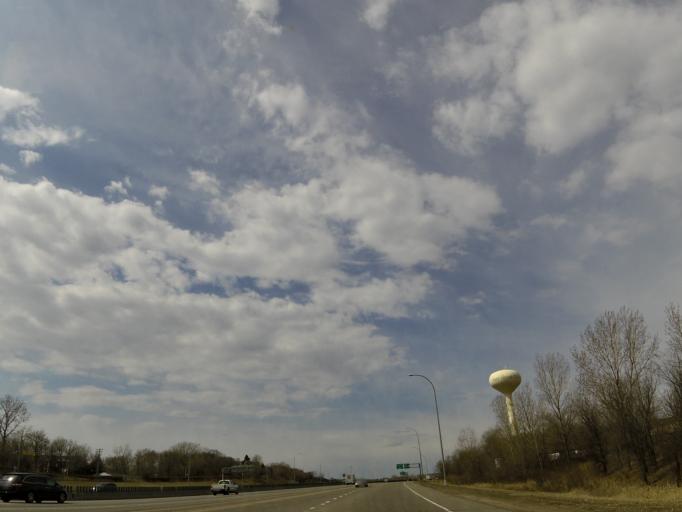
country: US
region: Minnesota
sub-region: Dakota County
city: South Saint Paul
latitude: 44.8751
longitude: -93.0655
